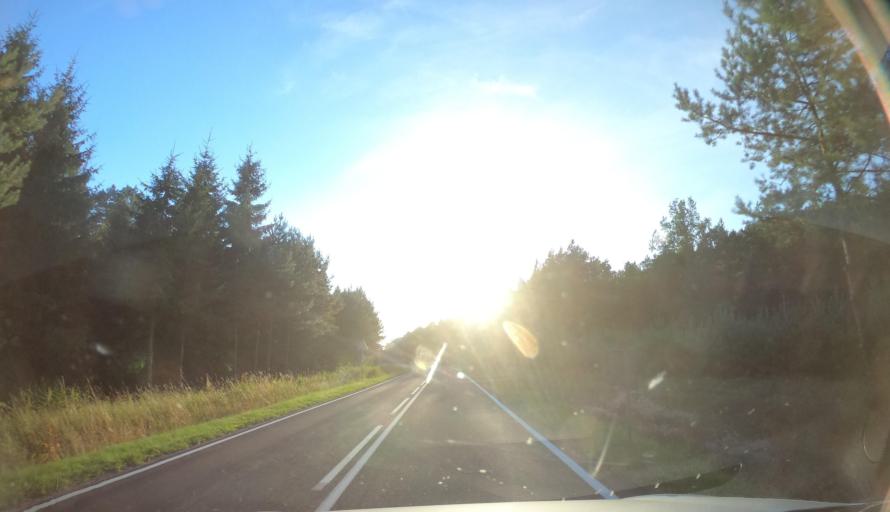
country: PL
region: Kujawsko-Pomorskie
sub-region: Powiat bydgoski
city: Koronowo
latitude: 53.3113
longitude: 18.0287
